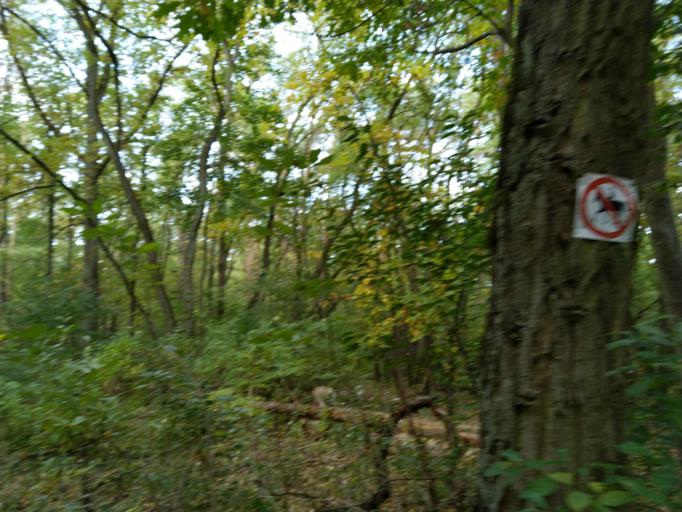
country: DE
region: Brandenburg
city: Schoneiche
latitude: 52.4737
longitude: 13.6782
